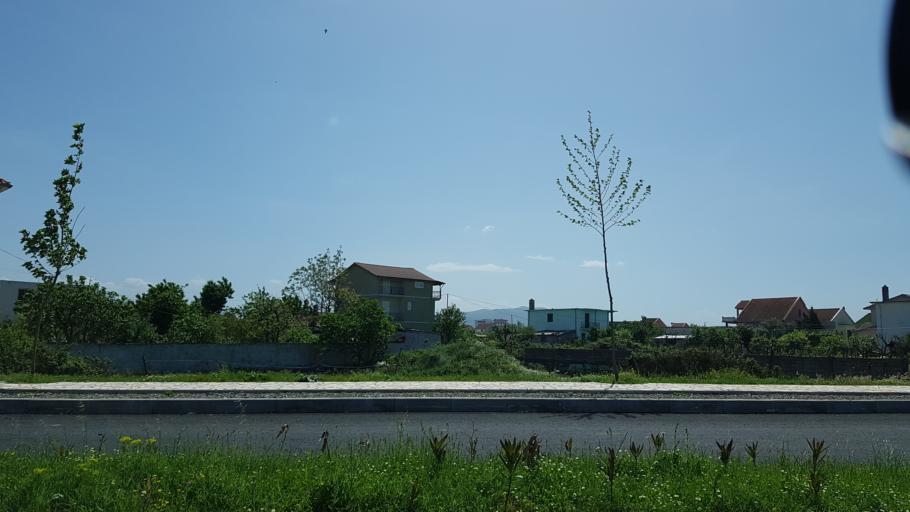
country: AL
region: Shkoder
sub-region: Rrethi i Shkodres
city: Shkoder
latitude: 42.0857
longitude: 19.5036
